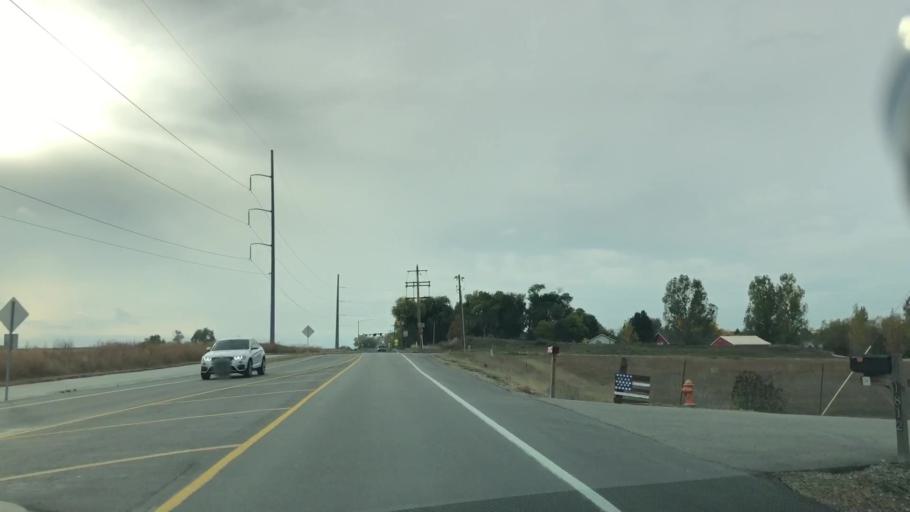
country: US
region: Colorado
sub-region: Larimer County
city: Loveland
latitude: 40.4656
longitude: -105.0452
